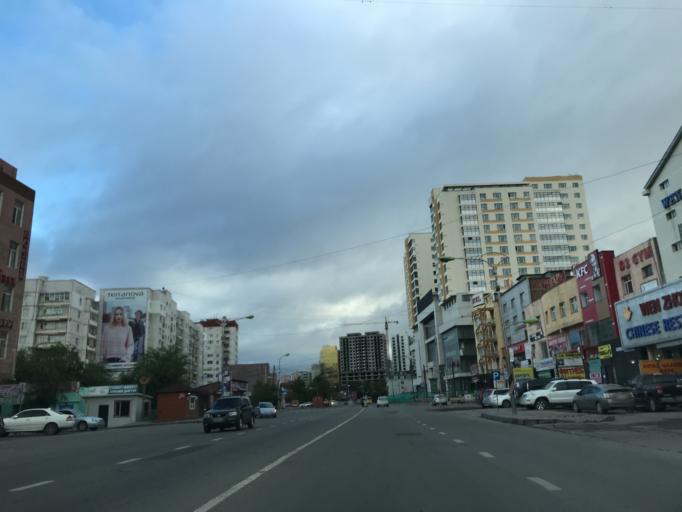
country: MN
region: Ulaanbaatar
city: Ulaanbaatar
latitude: 47.9140
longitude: 106.9439
